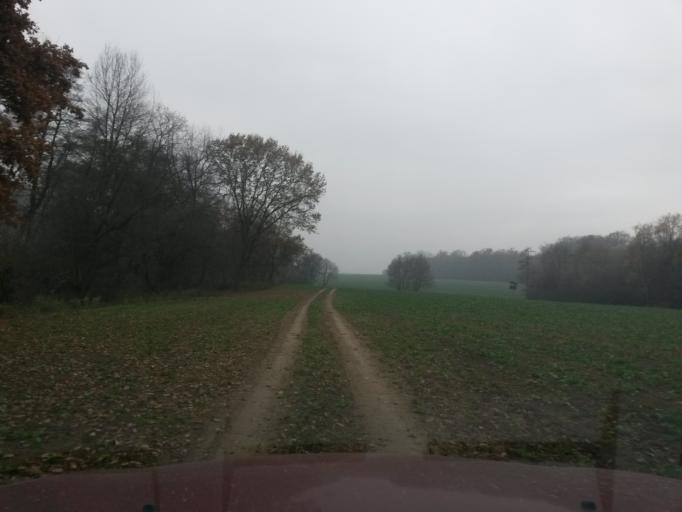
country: SK
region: Presovsky
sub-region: Okres Presov
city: Presov
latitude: 48.8925
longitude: 21.2979
